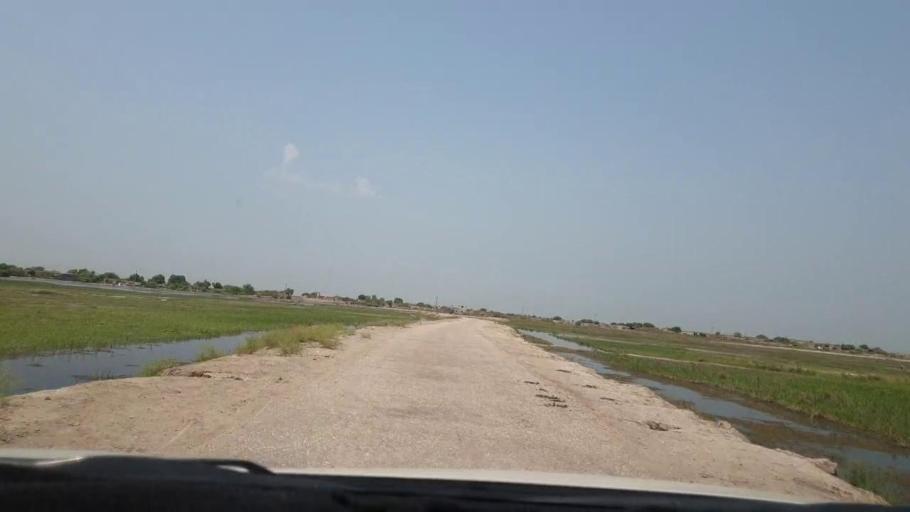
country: PK
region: Sindh
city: Radhan
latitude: 27.2452
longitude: 67.9957
